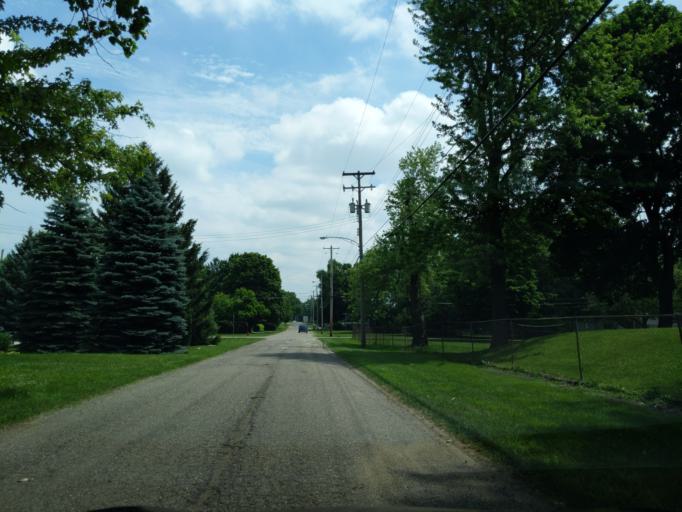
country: US
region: Michigan
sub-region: Ingham County
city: Lansing
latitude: 42.7678
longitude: -84.5474
